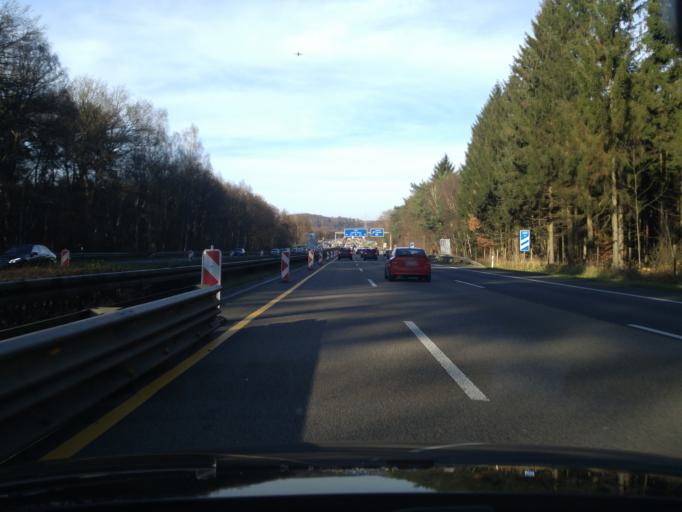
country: DE
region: North Rhine-Westphalia
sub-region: Regierungsbezirk Koln
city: Siegburg
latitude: 50.8176
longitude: 7.2104
